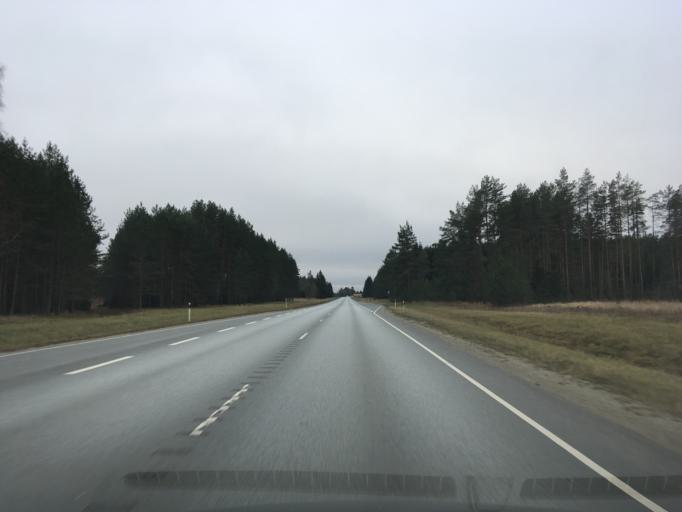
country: EE
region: Laeaene-Virumaa
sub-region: Viru-Nigula vald
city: Kunda
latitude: 59.3989
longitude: 26.6286
